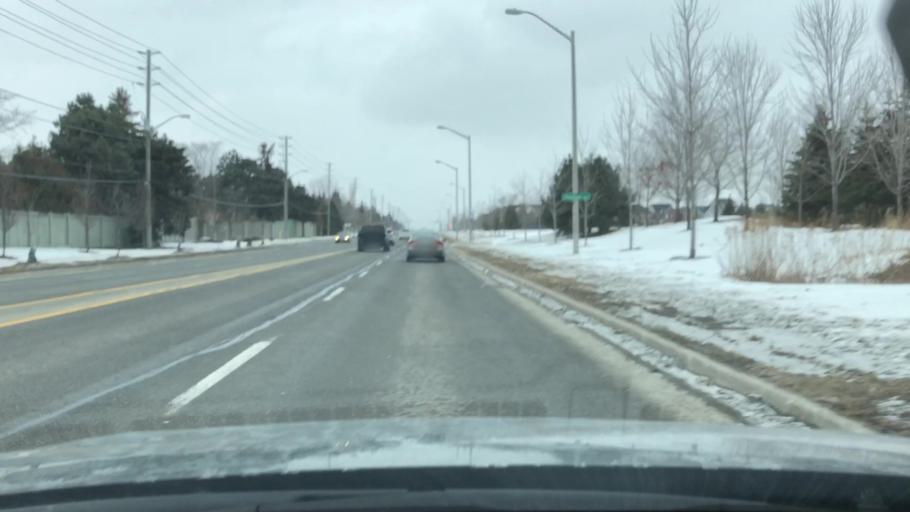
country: CA
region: Ontario
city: Markham
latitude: 43.8908
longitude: -79.2378
